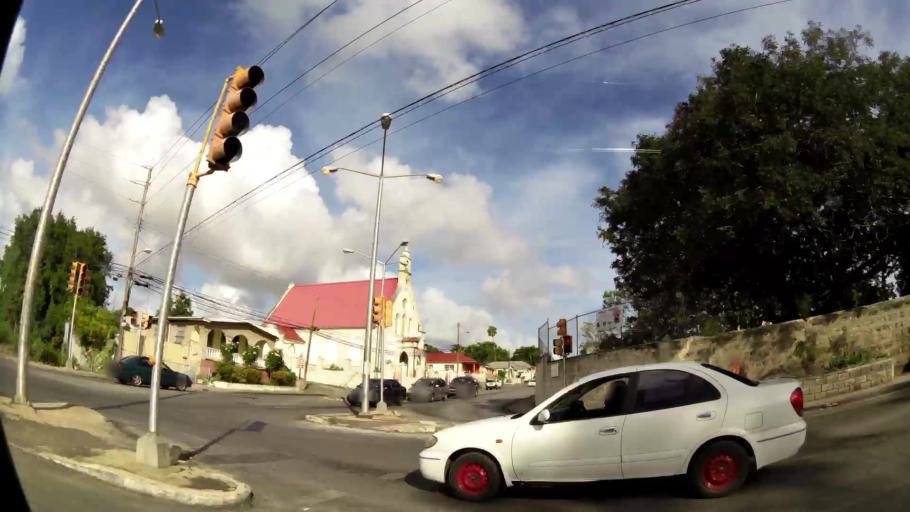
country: BB
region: Saint Michael
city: Bridgetown
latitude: 13.0873
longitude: -59.6006
